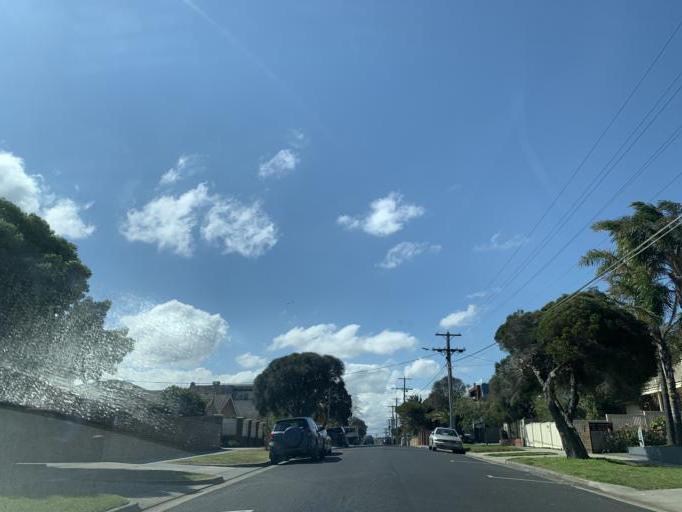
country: AU
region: Victoria
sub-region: Kingston
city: Parkdale
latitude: -37.9970
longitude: 145.0761
